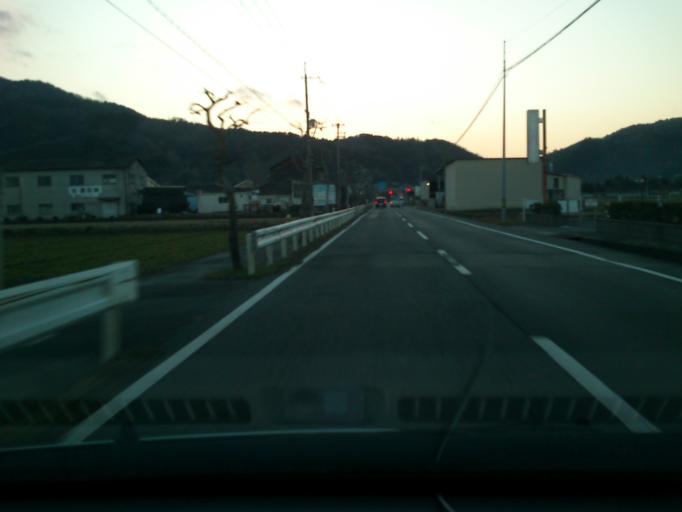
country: JP
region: Kyoto
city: Kameoka
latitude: 35.0505
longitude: 135.5390
